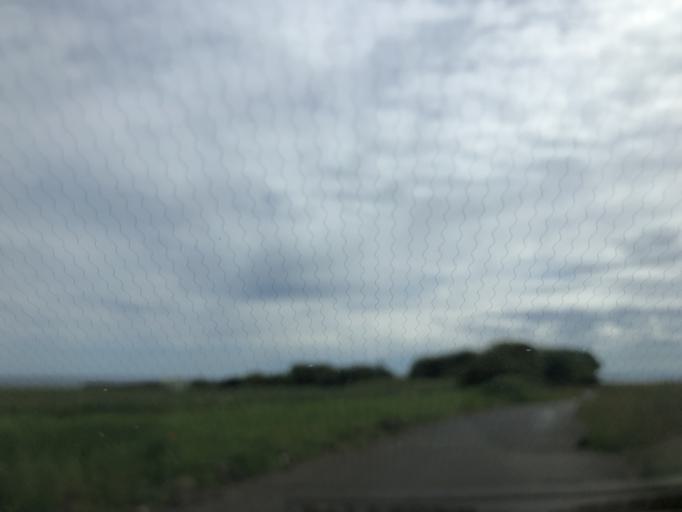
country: GB
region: Scotland
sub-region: Fife
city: Anstruther
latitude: 56.2730
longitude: -2.6006
